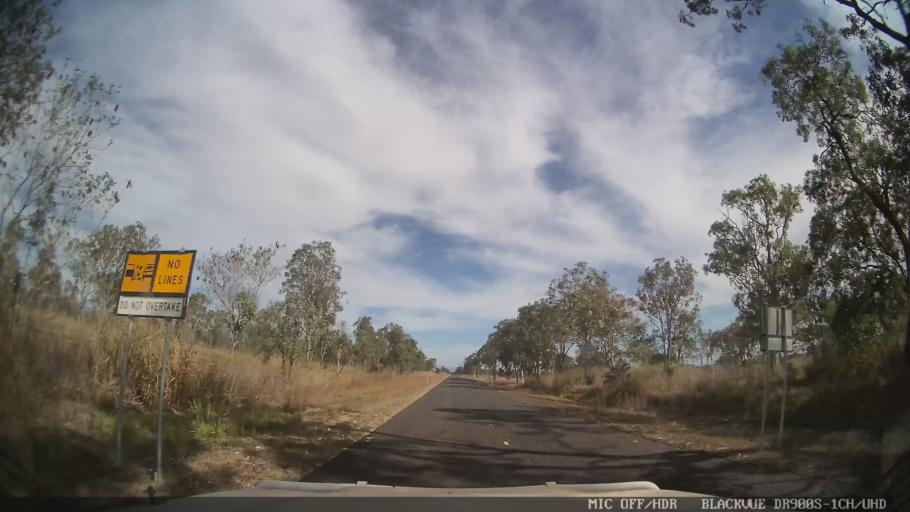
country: AU
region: Queensland
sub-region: Tablelands
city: Mareeba
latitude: -16.9428
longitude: 145.4163
